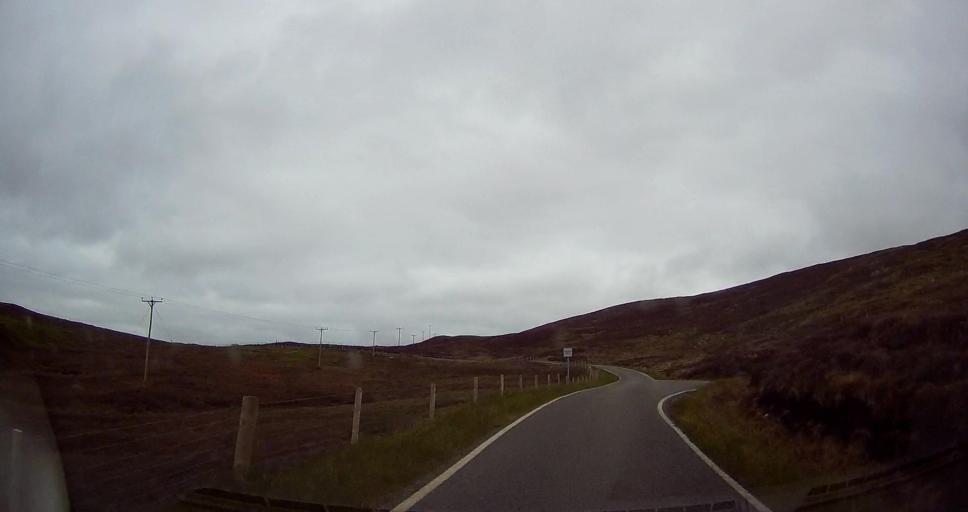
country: GB
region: Scotland
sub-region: Shetland Islands
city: Lerwick
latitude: 60.3083
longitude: -1.3382
